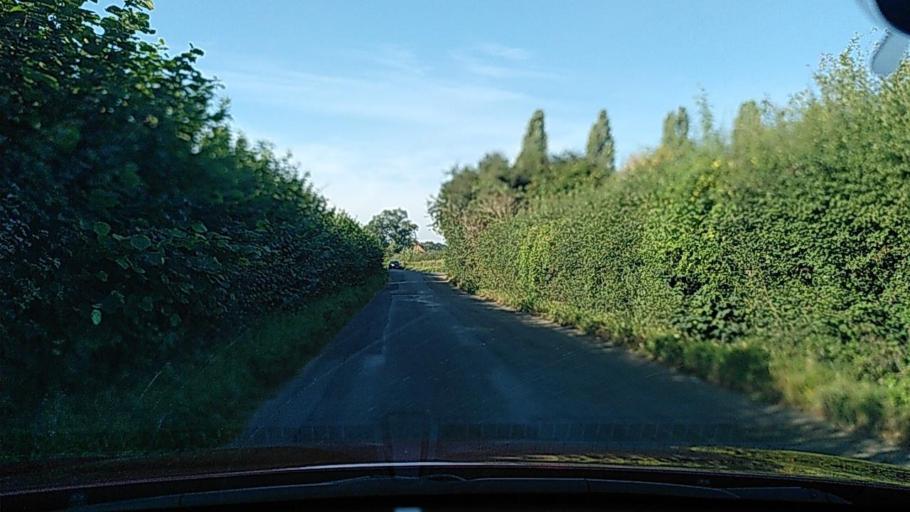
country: GB
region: England
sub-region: Oxfordshire
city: Sonning Common
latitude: 51.4929
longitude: -0.9532
